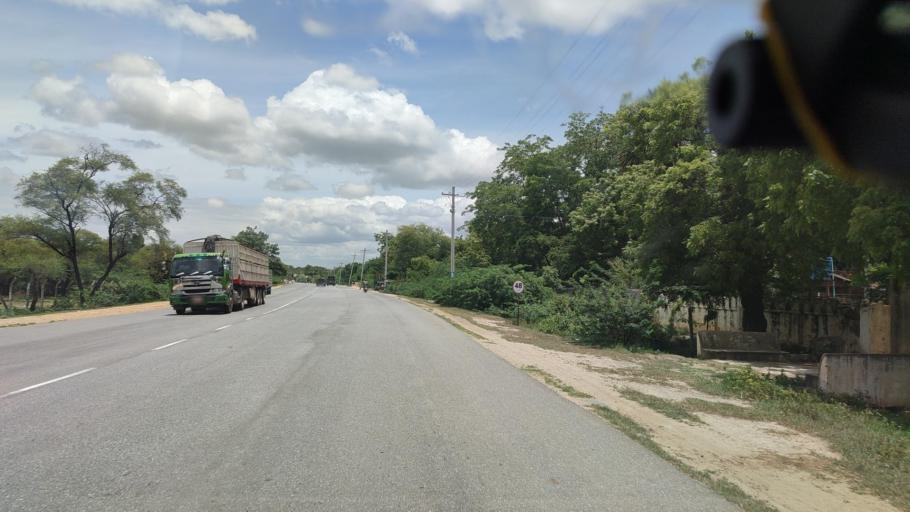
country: MM
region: Mandalay
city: Meiktila
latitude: 20.7263
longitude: 95.9340
